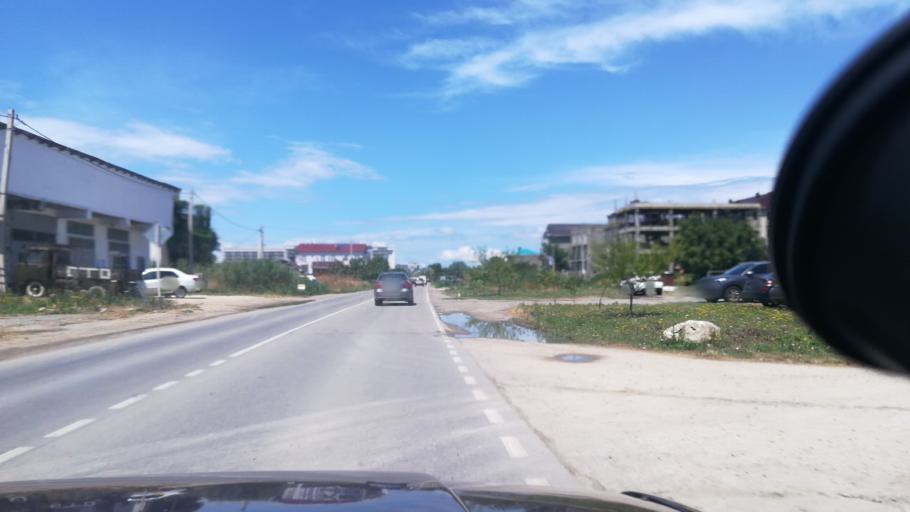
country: RU
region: Krasnodarskiy
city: Vityazevo
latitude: 44.9616
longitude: 37.2935
